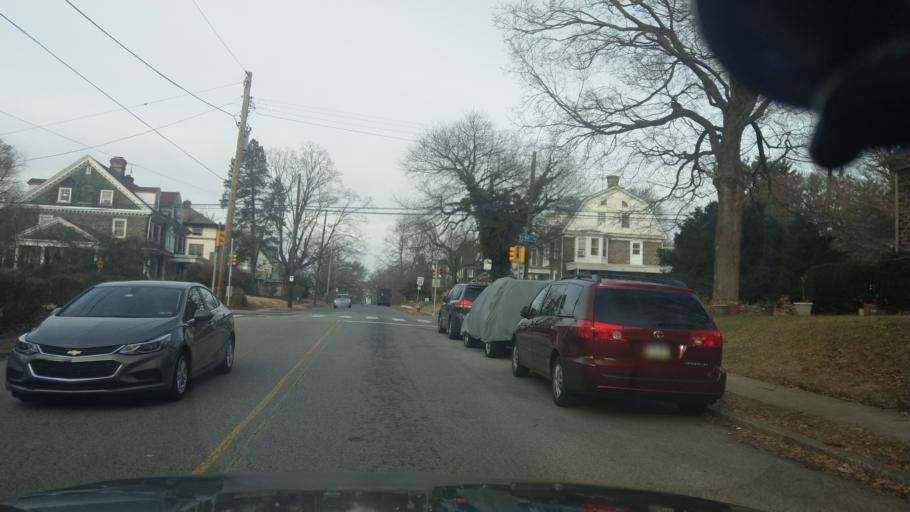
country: US
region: Pennsylvania
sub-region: Montgomery County
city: Wyncote
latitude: 40.0526
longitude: -75.1369
